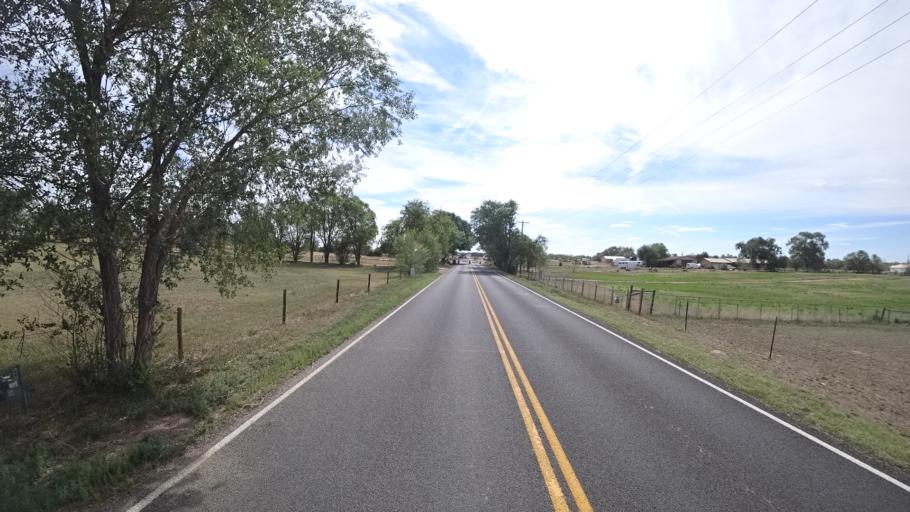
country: US
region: Colorado
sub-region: El Paso County
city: Fountain
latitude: 38.7085
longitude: -104.6767
